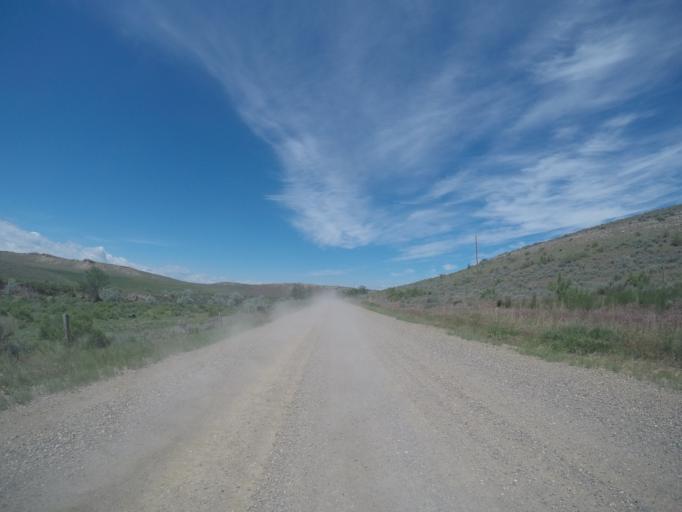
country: US
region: Montana
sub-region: Carbon County
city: Red Lodge
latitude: 45.2319
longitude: -108.8486
